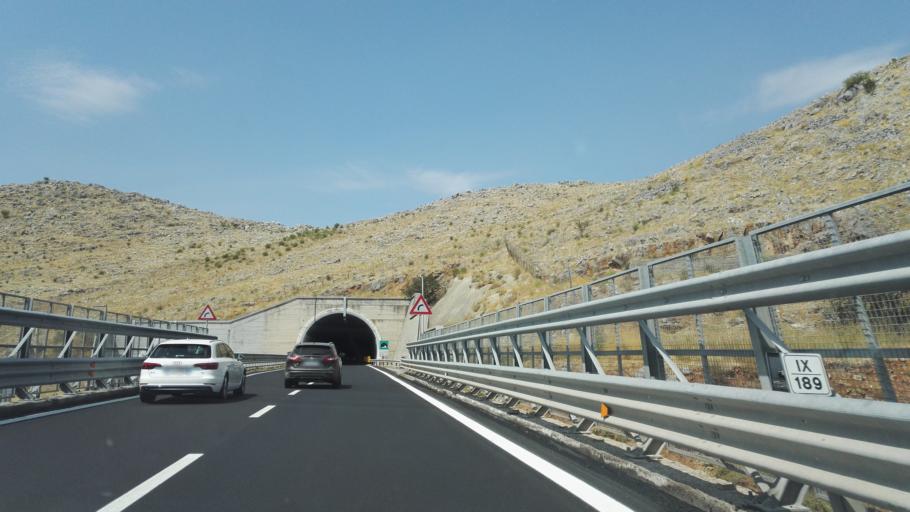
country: IT
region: Calabria
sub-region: Provincia di Cosenza
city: Castrovillari
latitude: 39.8491
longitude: 16.2141
